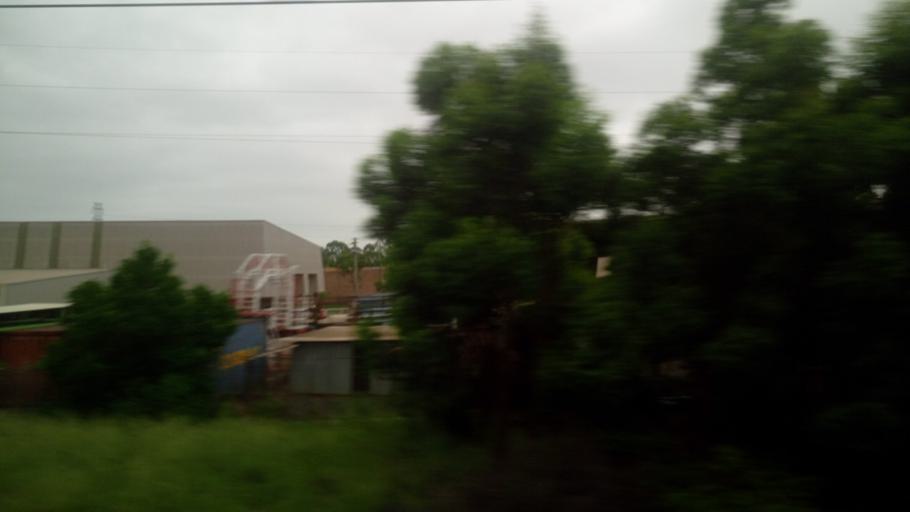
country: AU
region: New South Wales
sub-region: Blacktown
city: Mount Druitt
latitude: -33.7639
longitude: 150.7864
